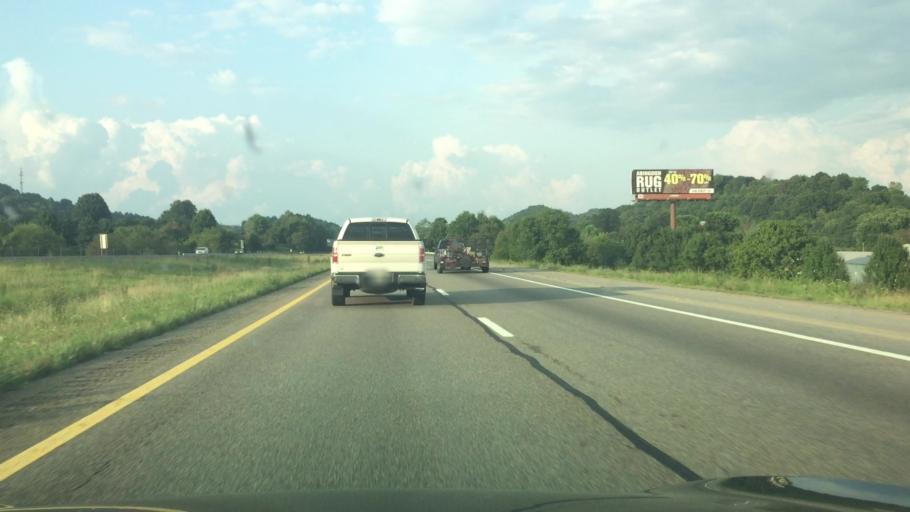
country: US
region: Tennessee
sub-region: Sullivan County
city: Blountville
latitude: 36.5233
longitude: -82.3994
